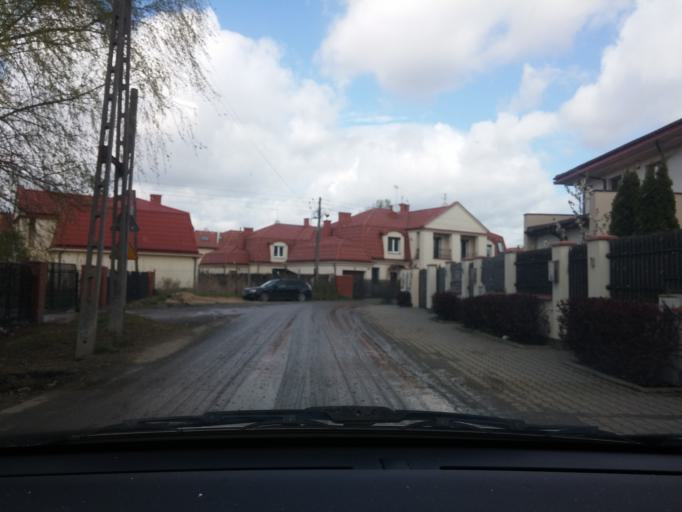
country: PL
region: Masovian Voivodeship
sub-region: Warszawa
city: Wawer
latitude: 52.1979
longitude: 21.1274
